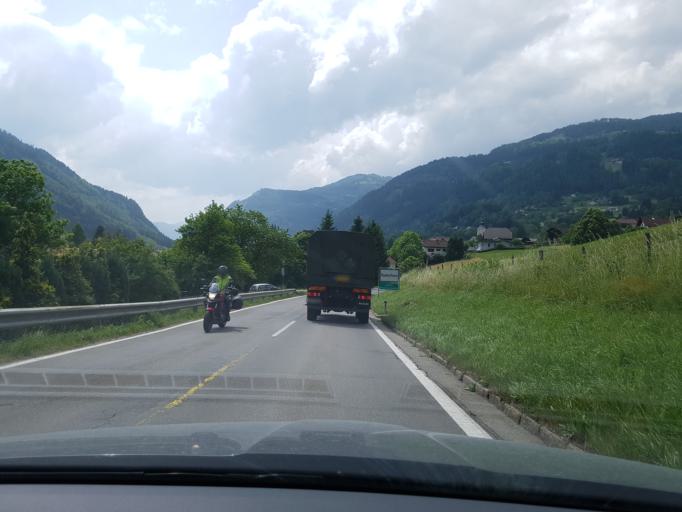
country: AT
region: Carinthia
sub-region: Politischer Bezirk Spittal an der Drau
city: Radenthein
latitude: 46.8016
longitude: 13.7124
